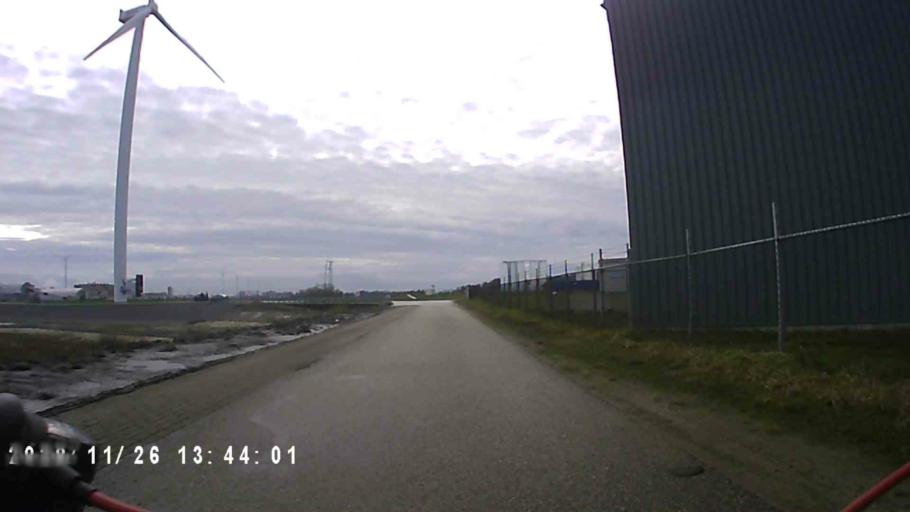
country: NL
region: Groningen
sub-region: Gemeente Delfzijl
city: Delfzijl
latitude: 53.3281
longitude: 6.9436
